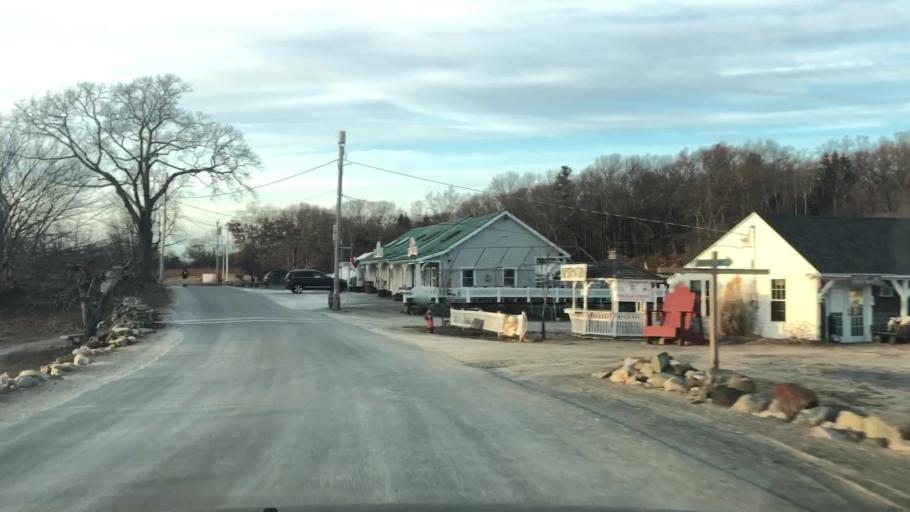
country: US
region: Massachusetts
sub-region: Essex County
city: North Andover
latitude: 42.6897
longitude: -71.0745
